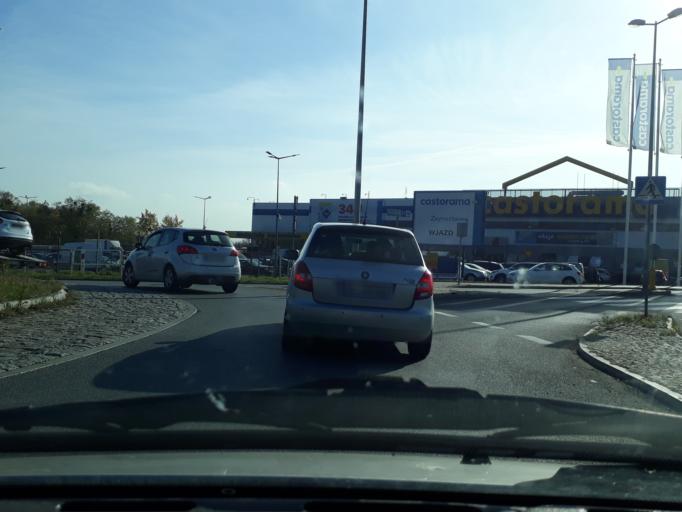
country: PL
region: Silesian Voivodeship
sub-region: Powiat tarnogorski
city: Tarnowskie Gory
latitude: 50.4378
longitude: 18.8419
